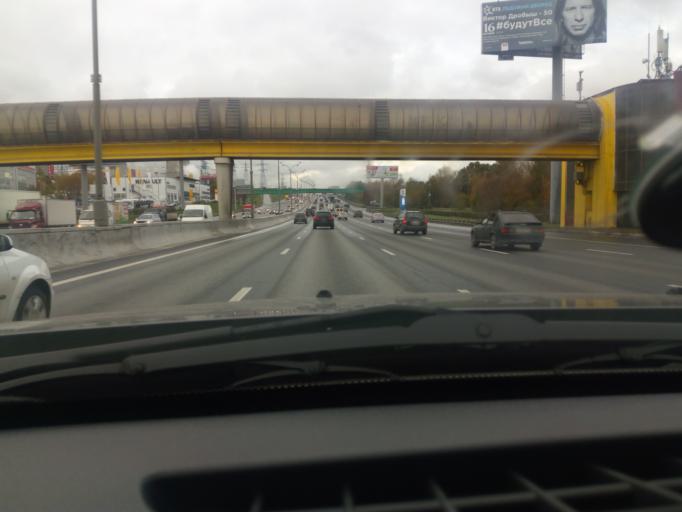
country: RU
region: Moskovskaya
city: Kotel'niki
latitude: 55.6461
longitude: 37.8281
